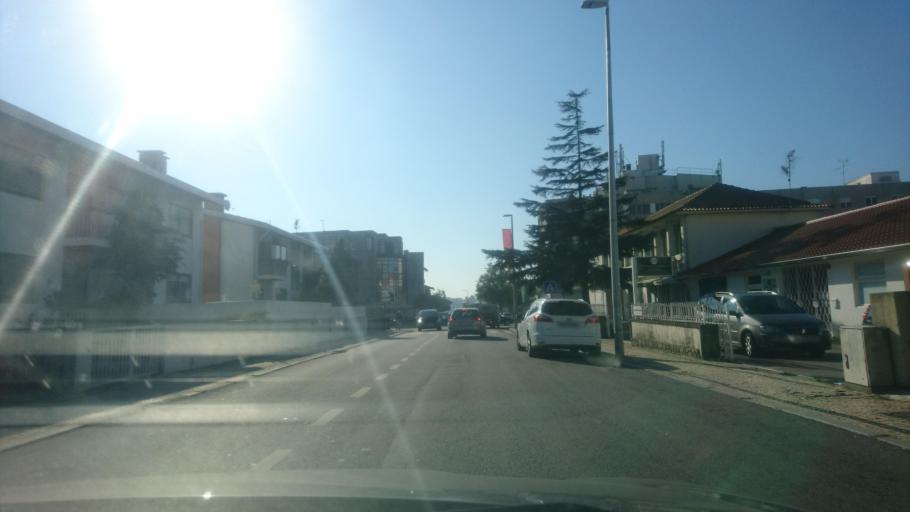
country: PT
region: Aveiro
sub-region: Santa Maria da Feira
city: Feira
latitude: 40.9264
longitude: -8.5478
